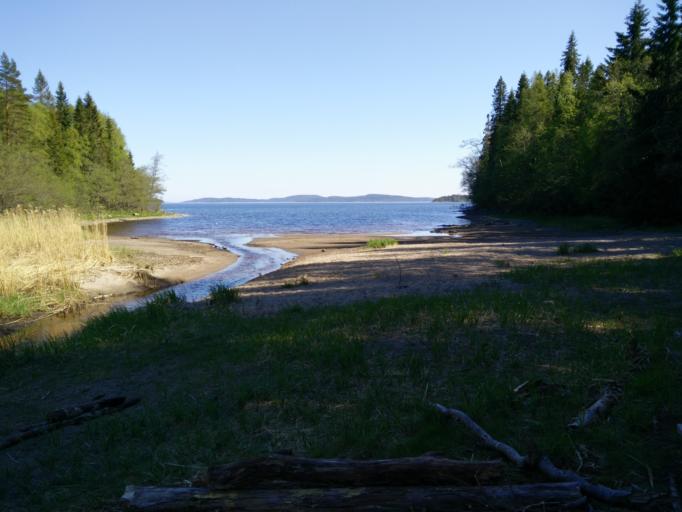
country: SE
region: Vaesternorrland
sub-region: OErnskoeldsviks Kommun
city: Kopmanholmen
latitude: 63.1287
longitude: 18.5248
